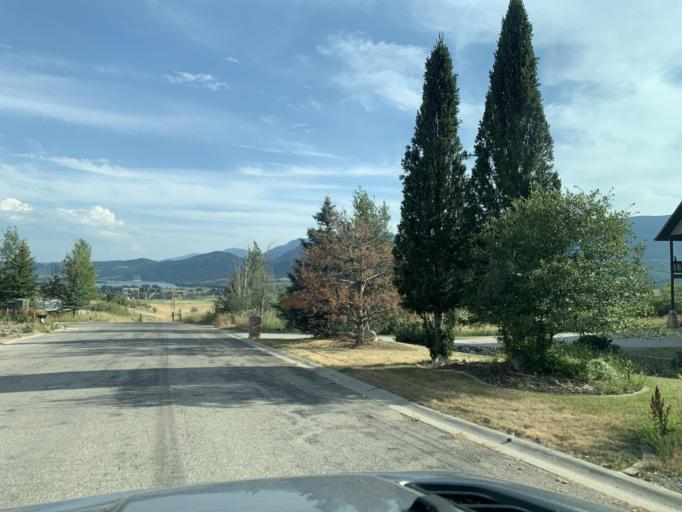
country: US
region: Utah
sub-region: Weber County
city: Wolf Creek
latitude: 41.3223
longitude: -111.8185
